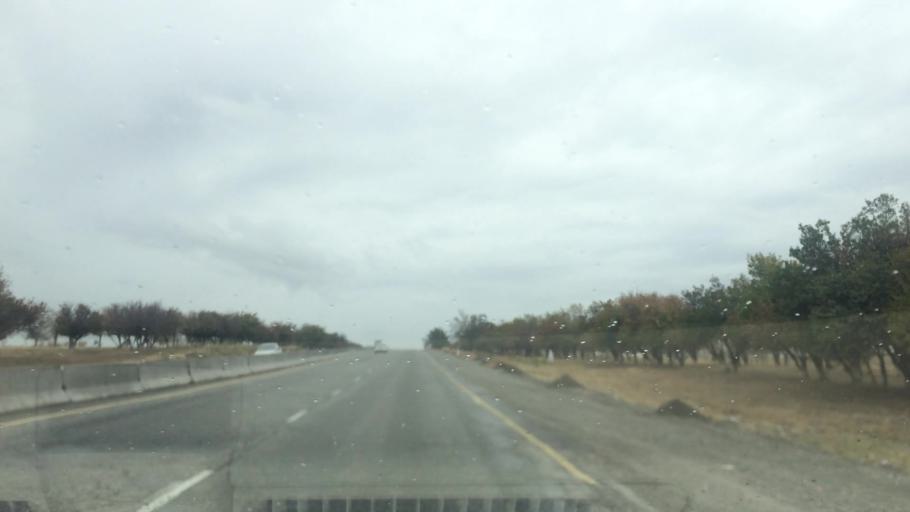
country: UZ
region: Samarqand
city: Bulung'ur
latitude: 39.8610
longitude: 67.4705
